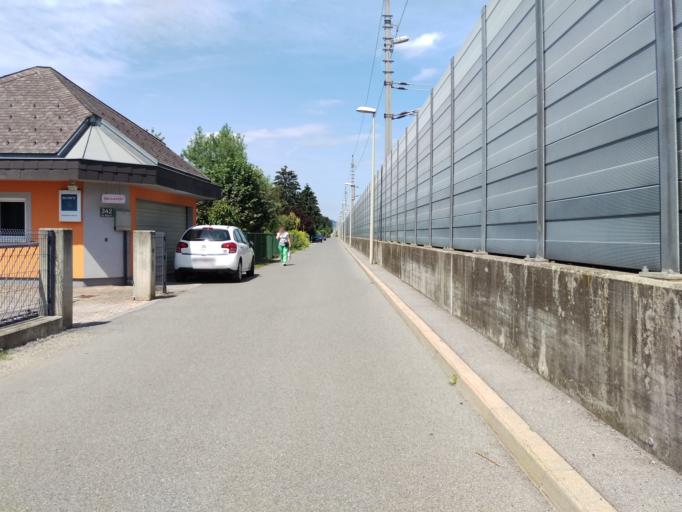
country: AT
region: Styria
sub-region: Politischer Bezirk Graz-Umgebung
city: Feldkirchen bei Graz
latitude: 47.0209
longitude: 15.4351
